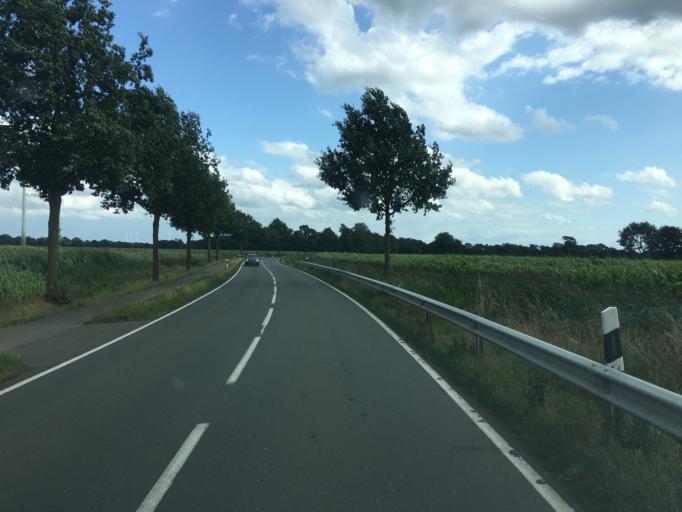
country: DE
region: Lower Saxony
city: Friesoythe
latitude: 53.0607
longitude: 7.8490
